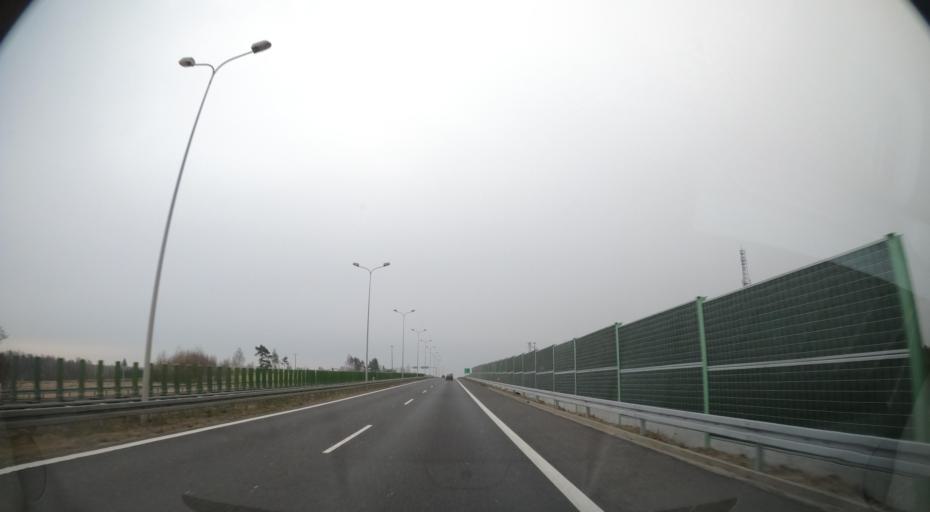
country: PL
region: Masovian Voivodeship
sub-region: Powiat grojecki
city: Goszczyn
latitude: 51.7329
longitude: 20.9157
